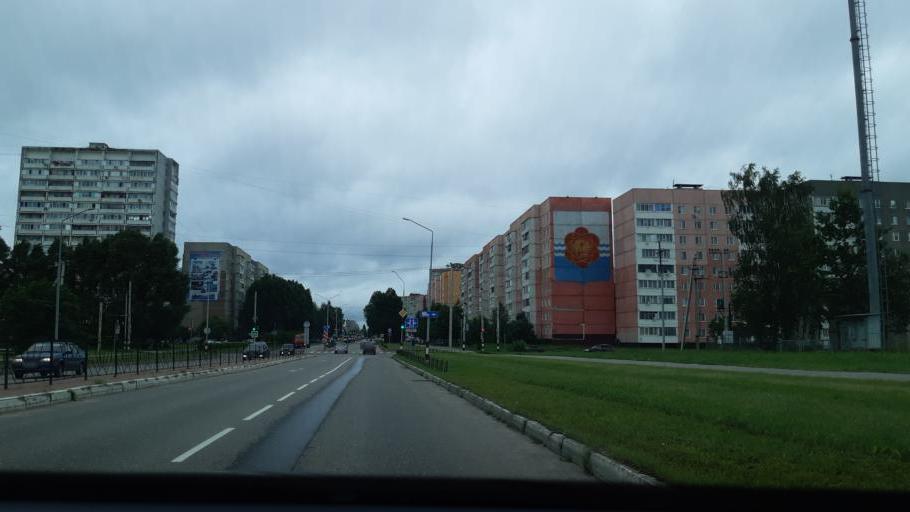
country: RU
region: Smolensk
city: Desnogorsk
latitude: 54.1464
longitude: 33.2828
